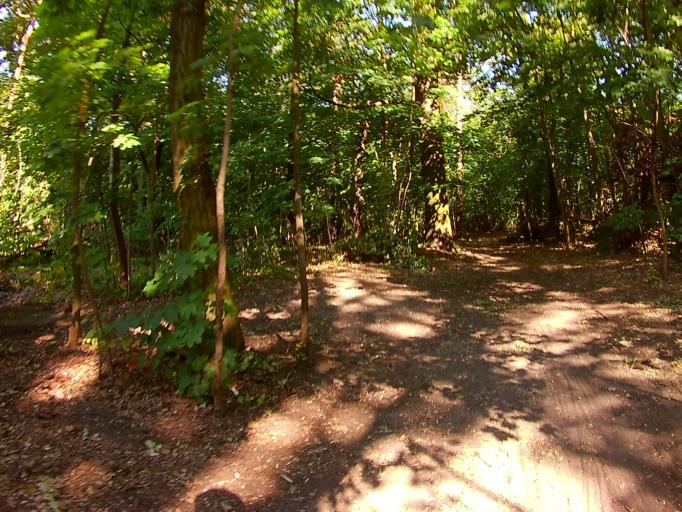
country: DE
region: Berlin
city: Grunau
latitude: 52.4088
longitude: 13.5825
